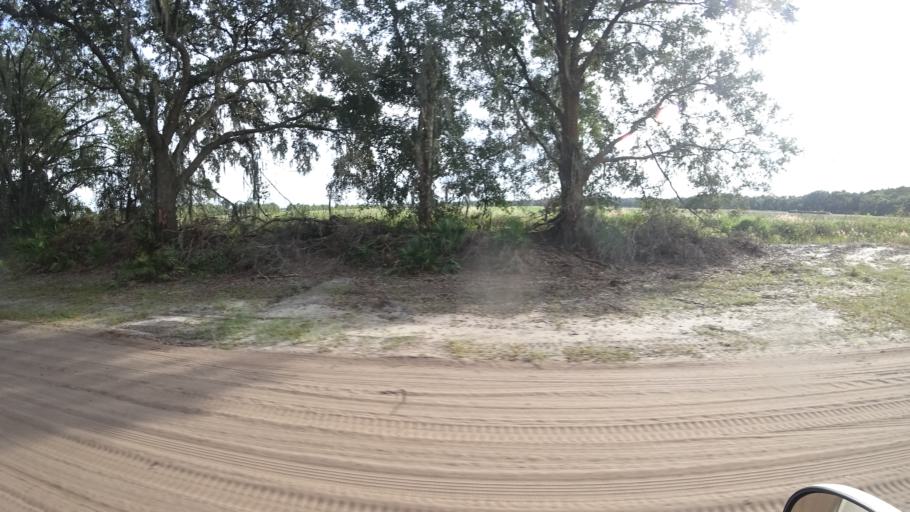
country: US
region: Florida
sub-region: Hillsborough County
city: Wimauma
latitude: 27.5963
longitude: -82.1397
